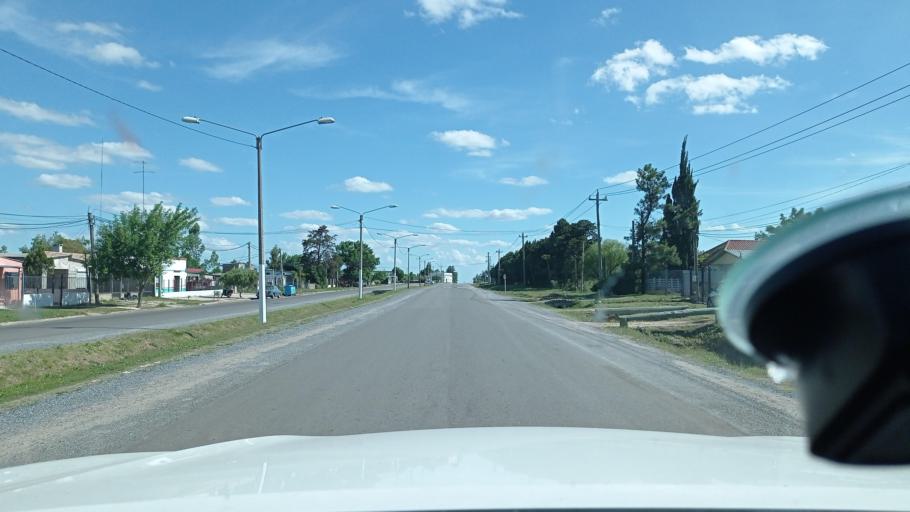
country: UY
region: Florida
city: Florida
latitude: -34.0883
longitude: -56.2380
